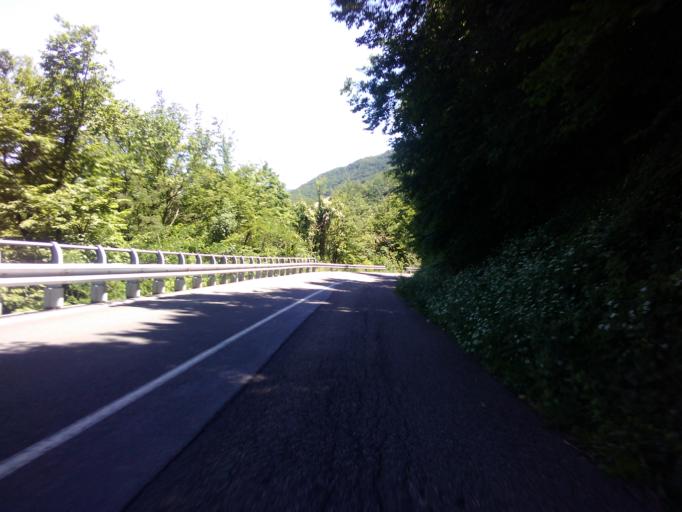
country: IT
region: Emilia-Romagna
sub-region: Provincia di Parma
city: Terenzo
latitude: 44.5859
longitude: 10.0922
